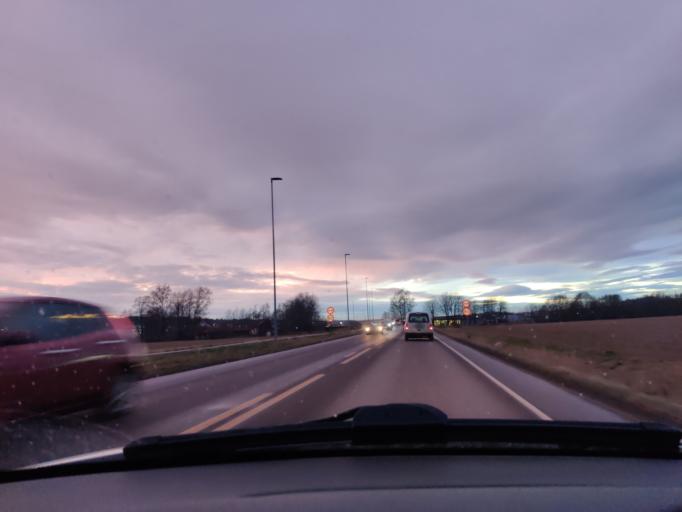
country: NO
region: Vestfold
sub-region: Tonsberg
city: Tonsberg
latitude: 59.2820
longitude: 10.3742
